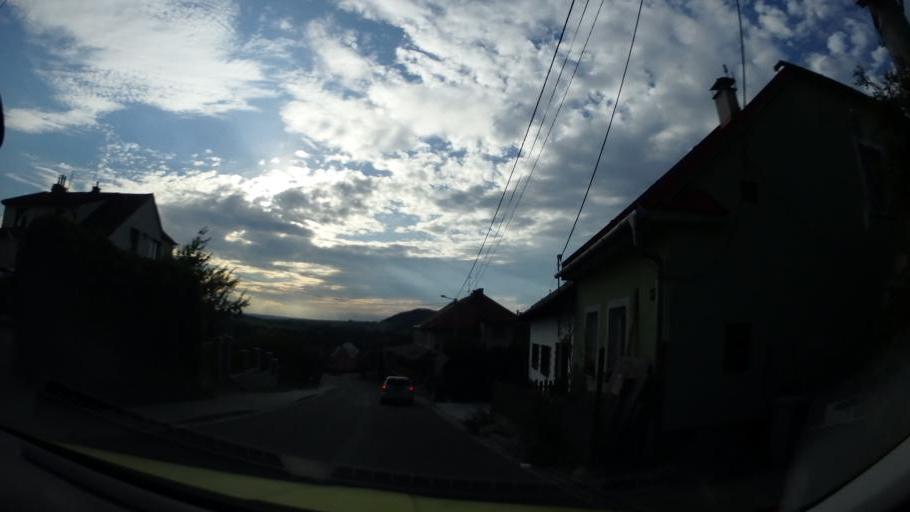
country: CZ
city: Stramberk
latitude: 49.5927
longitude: 18.1129
